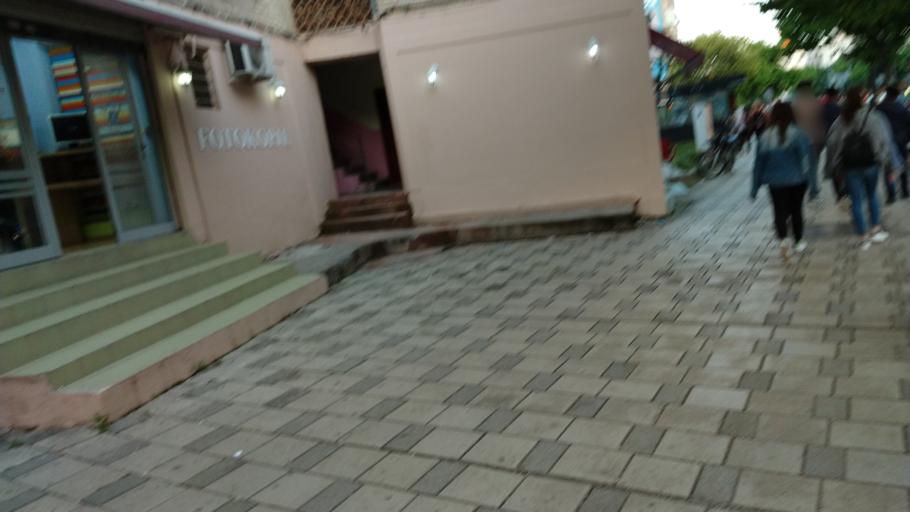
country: AL
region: Tirane
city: Tirana
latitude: 41.3286
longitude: 19.8028
